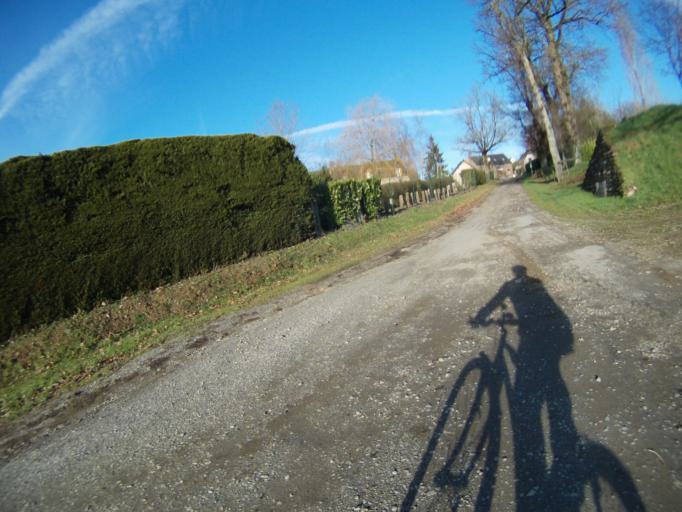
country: FR
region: Brittany
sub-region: Departement d'Ille-et-Vilaine
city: Chanteloup
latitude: 47.9268
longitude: -1.6131
